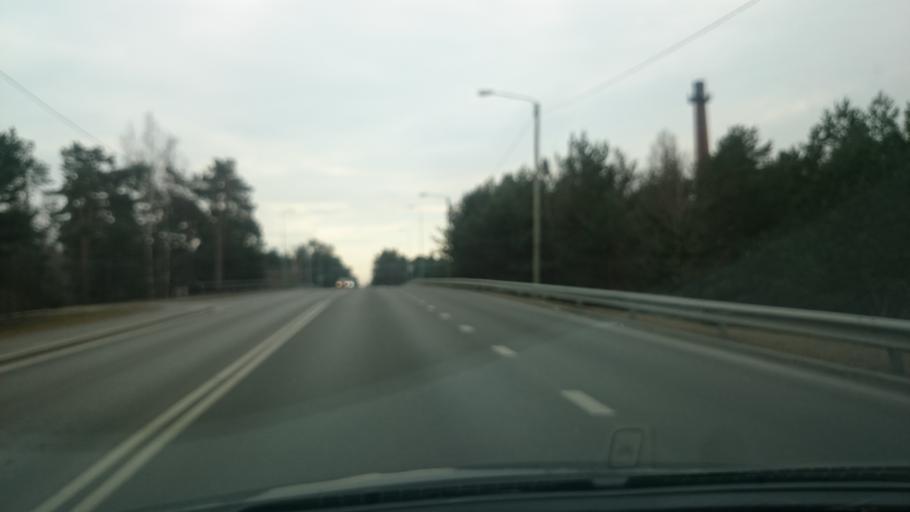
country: EE
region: Harju
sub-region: Saue vald
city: Laagri
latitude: 59.3855
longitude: 24.6397
